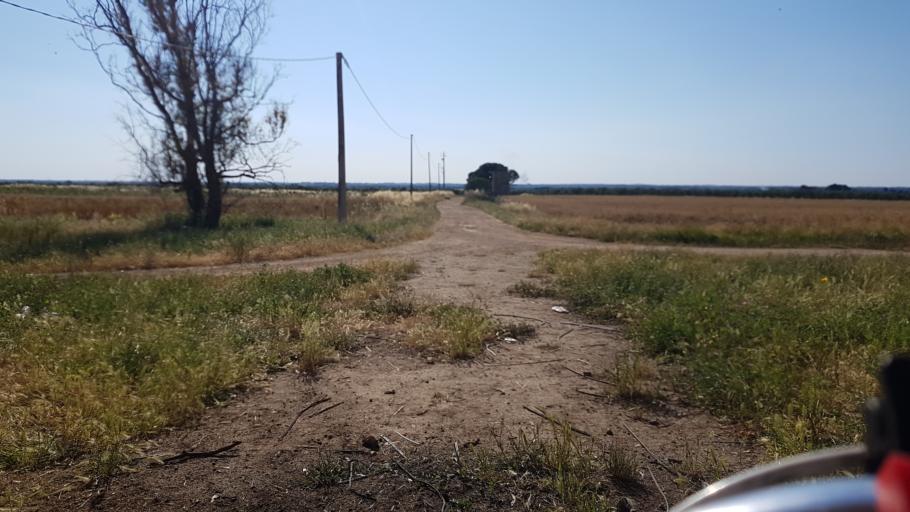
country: IT
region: Apulia
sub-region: Provincia di Brindisi
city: Mesagne
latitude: 40.6442
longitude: 17.8180
